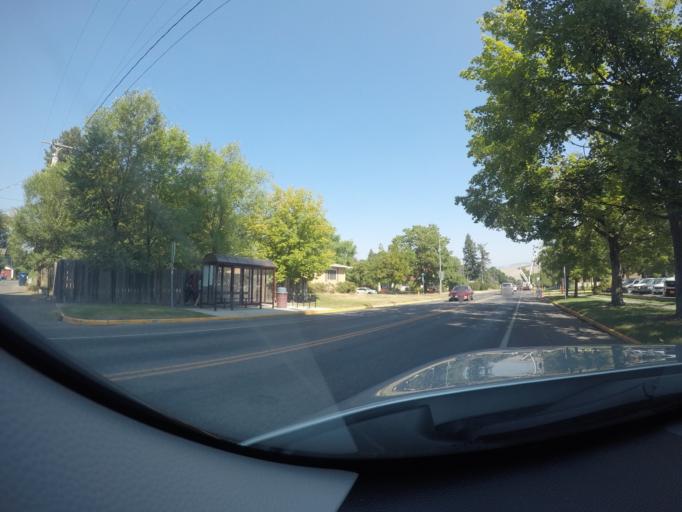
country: US
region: Montana
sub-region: Missoula County
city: Missoula
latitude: 46.8616
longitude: -113.9892
